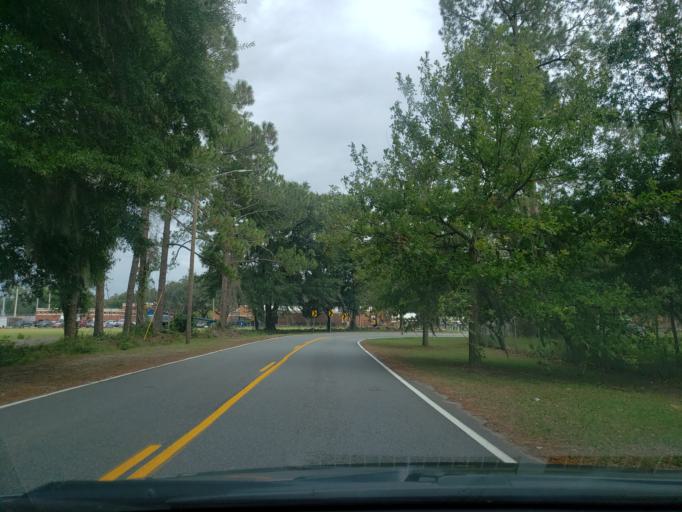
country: US
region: Georgia
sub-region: Chatham County
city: Isle of Hope
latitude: 32.0106
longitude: -81.0952
